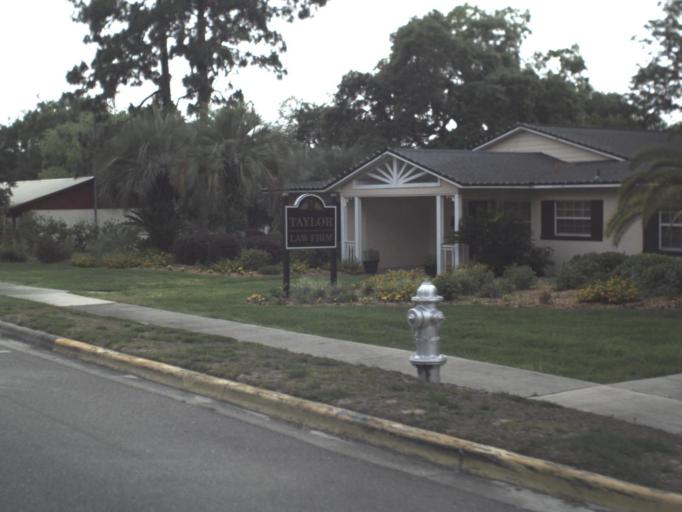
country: US
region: Florida
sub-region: Clay County
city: Keystone Heights
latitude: 29.7825
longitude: -82.0309
